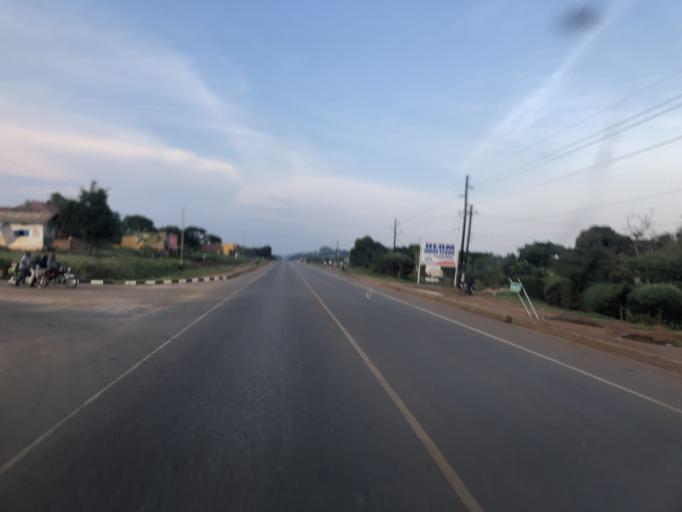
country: UG
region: Central Region
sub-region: Mpigi District
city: Mpigi
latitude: 0.2081
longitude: 32.3164
